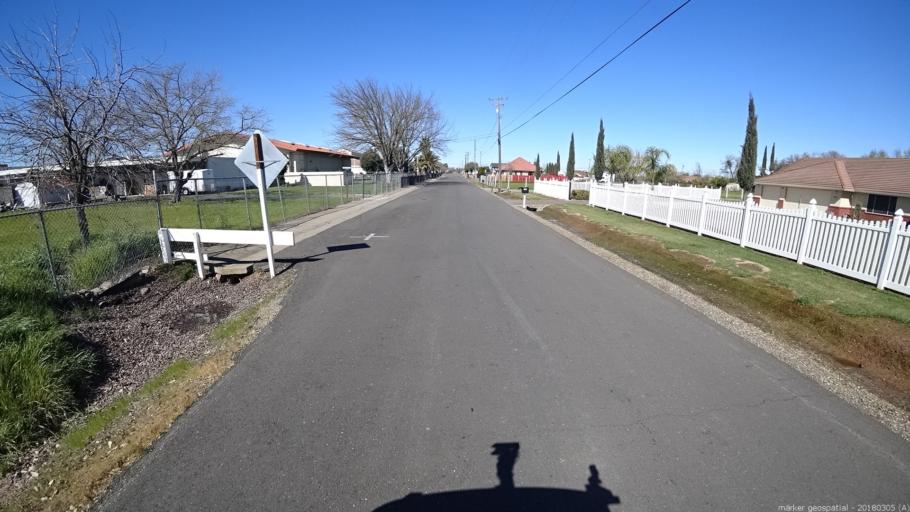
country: US
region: California
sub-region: Sacramento County
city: Florin
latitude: 38.4940
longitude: -121.3790
